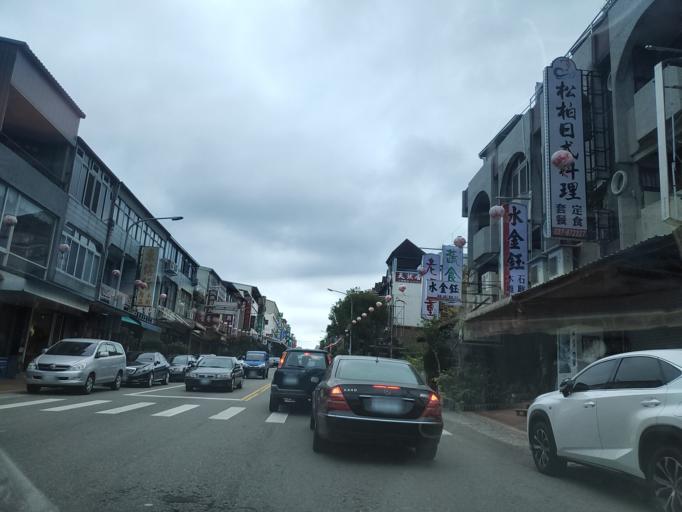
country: TW
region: Taiwan
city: Fengyuan
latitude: 24.4025
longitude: 120.7641
